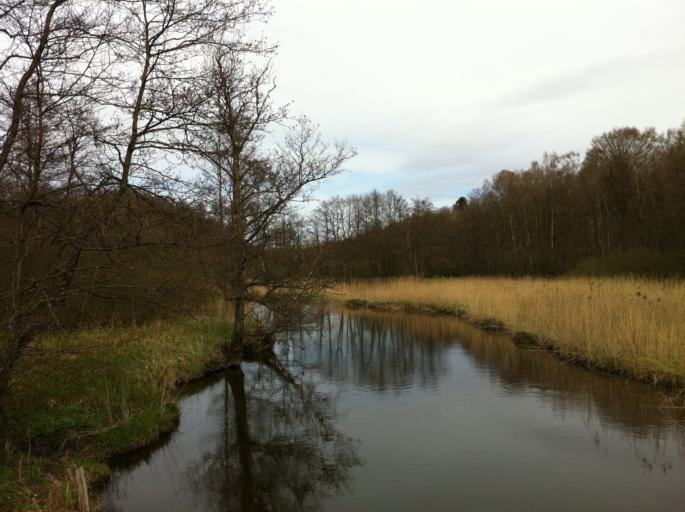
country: SE
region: Skane
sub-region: Eslovs Kommun
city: Stehag
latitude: 56.0131
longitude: 13.3879
